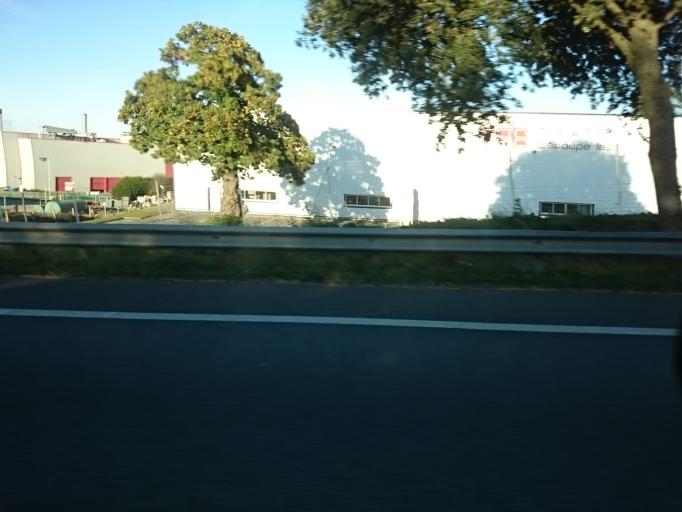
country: FR
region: Brittany
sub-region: Departement des Cotes-d'Armor
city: Lamballe
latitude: 48.4615
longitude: -2.5392
